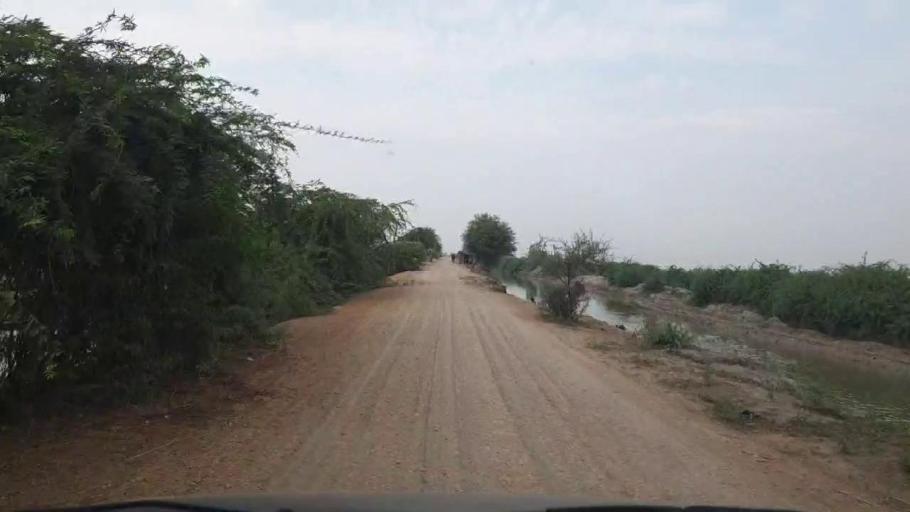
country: PK
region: Sindh
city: Kario
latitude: 24.6068
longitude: 68.5963
